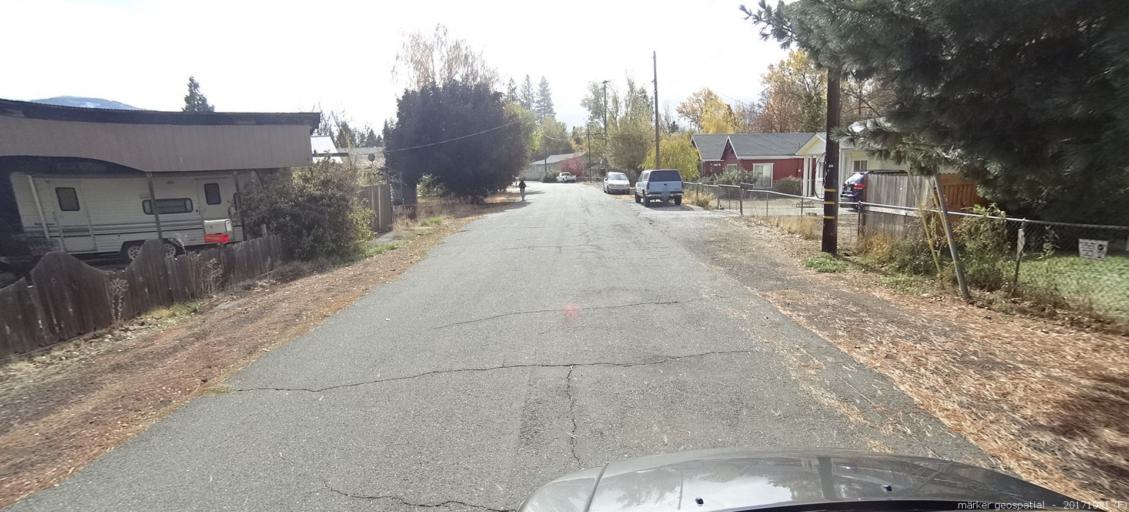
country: US
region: California
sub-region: Shasta County
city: Burney
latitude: 40.8831
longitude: -121.6681
